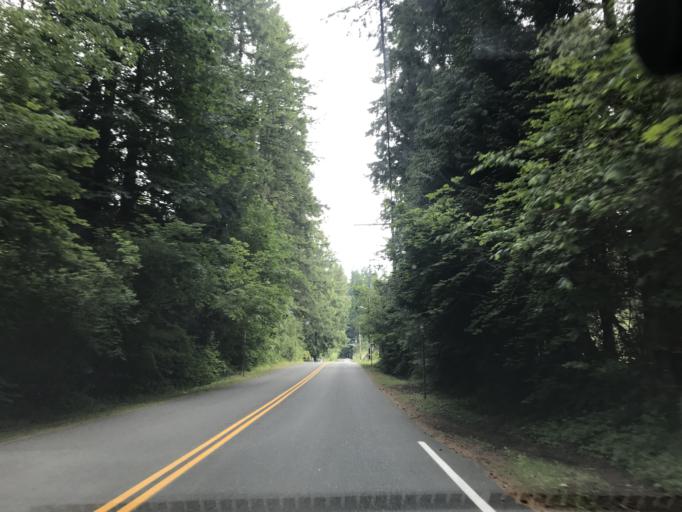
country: US
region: Washington
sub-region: King County
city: Maple Valley
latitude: 47.3793
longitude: -122.0427
